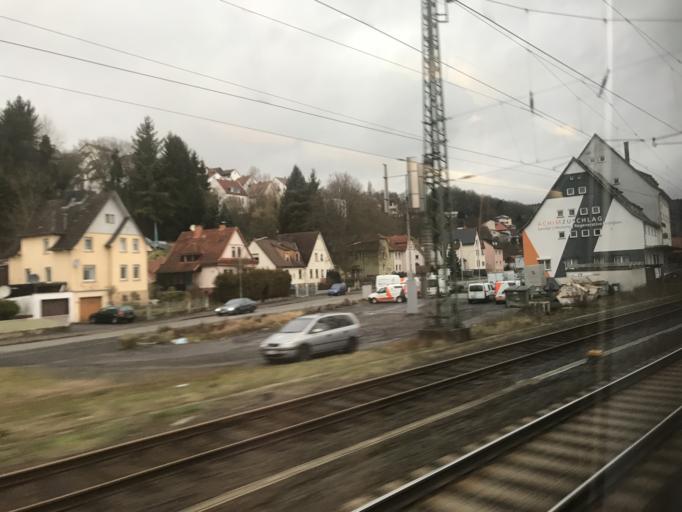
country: DE
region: Hesse
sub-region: Regierungsbezirk Kassel
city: Bad Hersfeld
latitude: 50.8759
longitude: 9.7208
